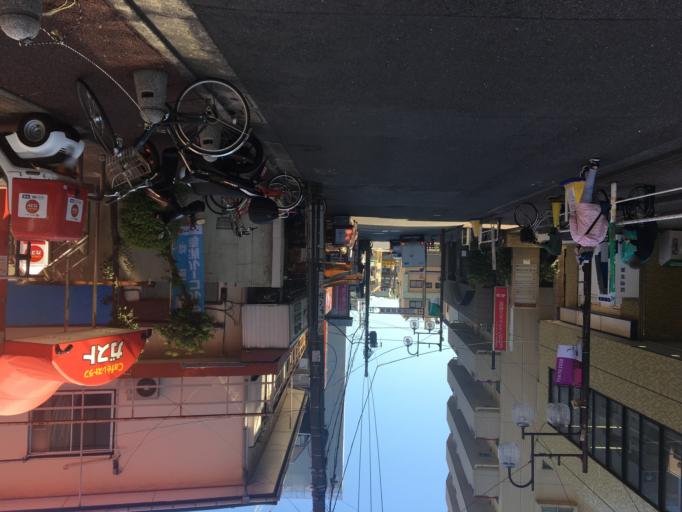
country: JP
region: Saitama
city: Shimotoda
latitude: 35.7617
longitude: 139.6751
